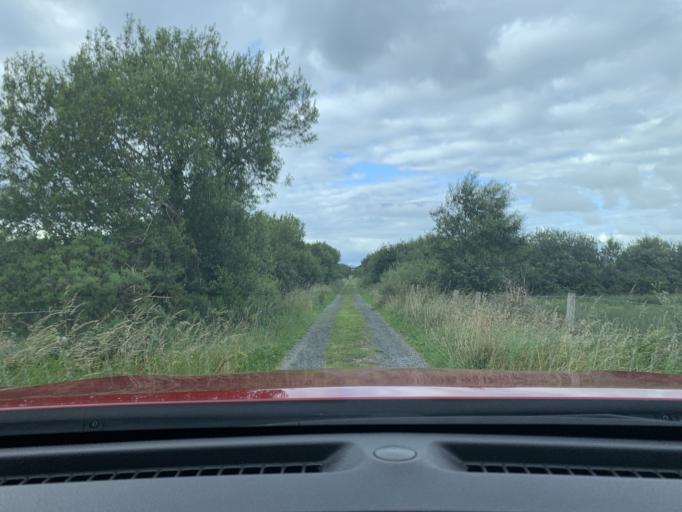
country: IE
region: Connaught
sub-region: County Leitrim
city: Kinlough
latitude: 54.4577
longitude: -8.3571
